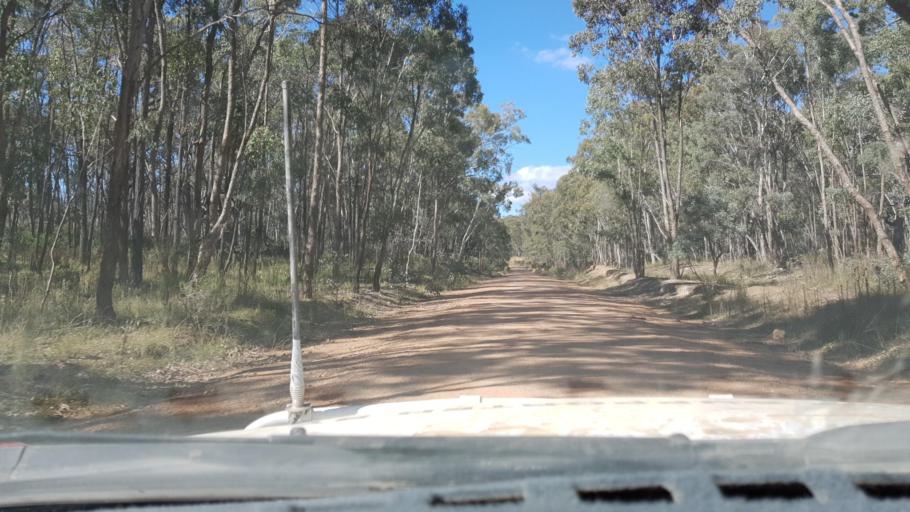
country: AU
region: New South Wales
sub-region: Tamworth Municipality
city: Manilla
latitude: -30.4558
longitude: 150.8802
